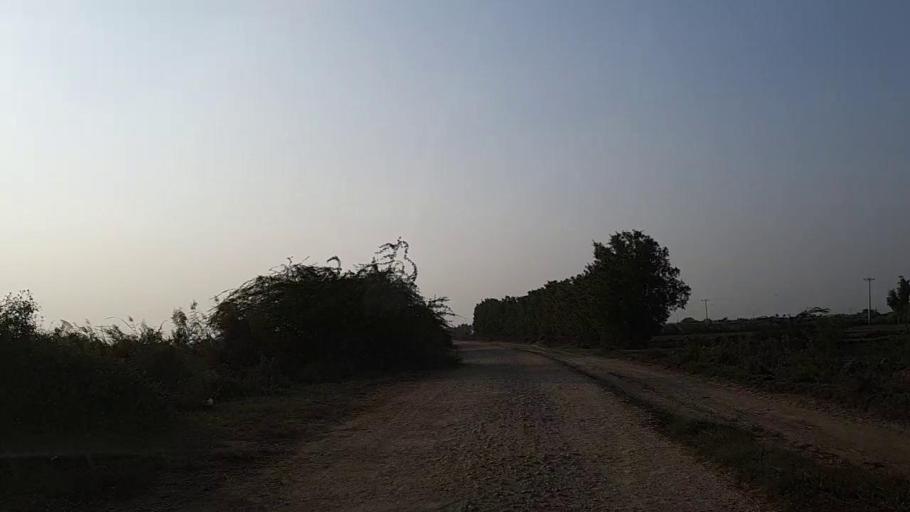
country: PK
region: Sindh
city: Thatta
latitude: 24.6925
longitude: 67.7893
